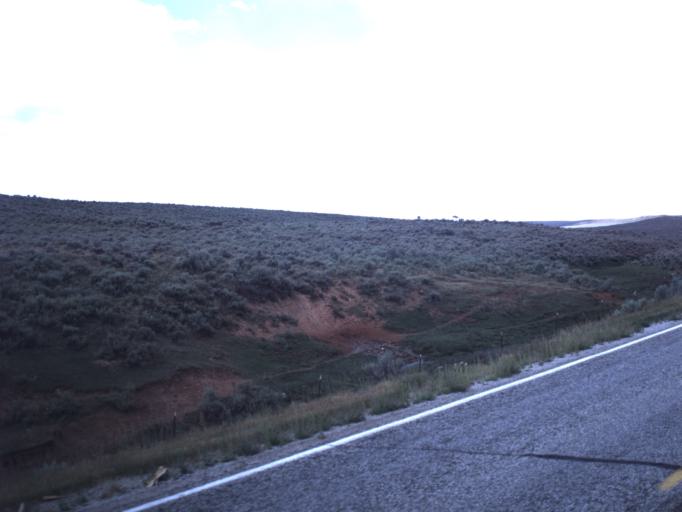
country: US
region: Utah
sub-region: Rich County
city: Randolph
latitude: 41.7899
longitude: -111.2137
